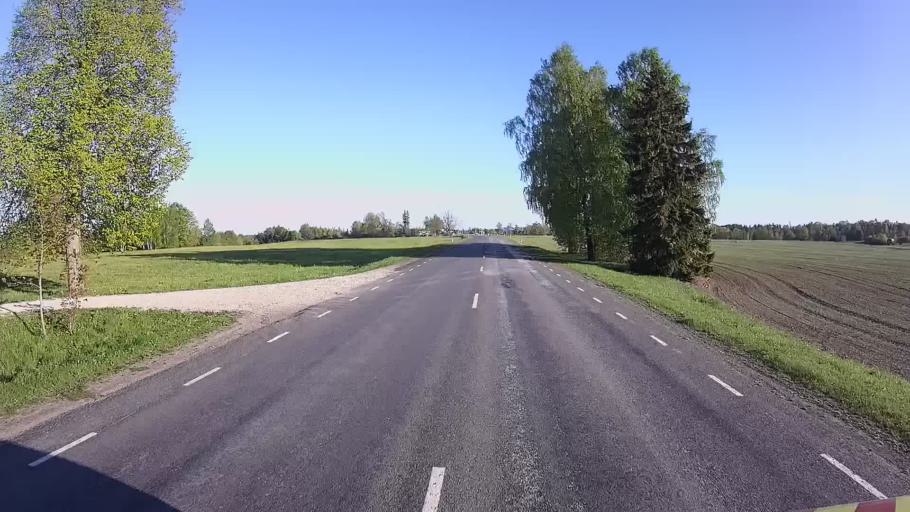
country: EE
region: Viljandimaa
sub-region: Viljandi linn
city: Viljandi
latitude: 58.3947
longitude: 25.5925
